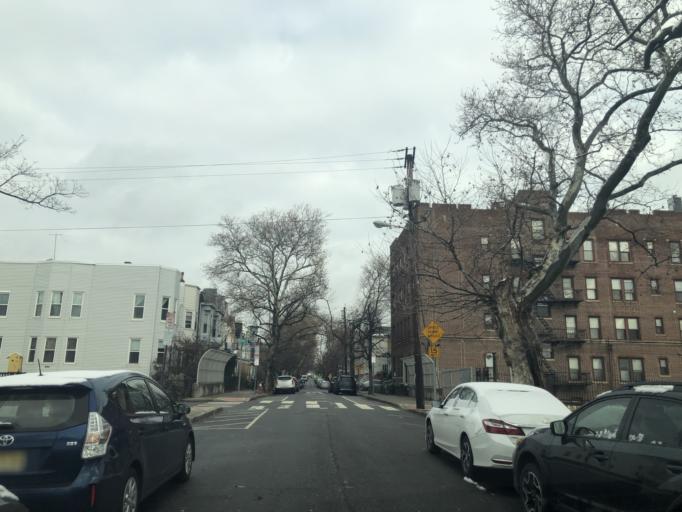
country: US
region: New Jersey
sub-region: Hudson County
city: Hoboken
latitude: 40.7449
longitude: -74.0427
